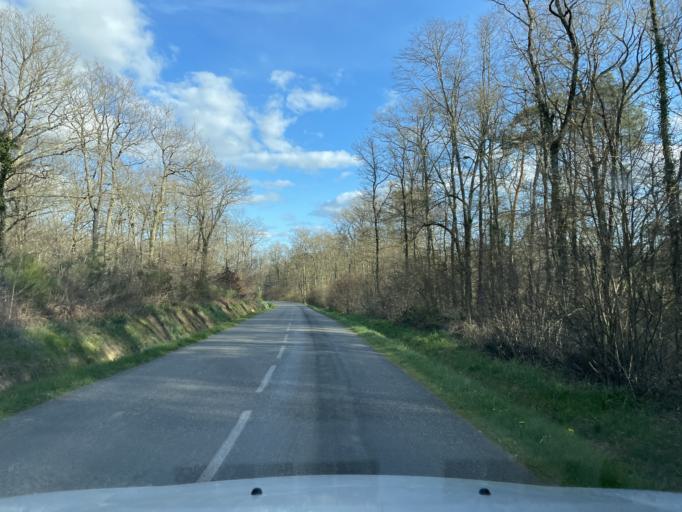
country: FR
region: Midi-Pyrenees
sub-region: Departement de la Haute-Garonne
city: Leguevin
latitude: 43.6173
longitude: 1.1940
